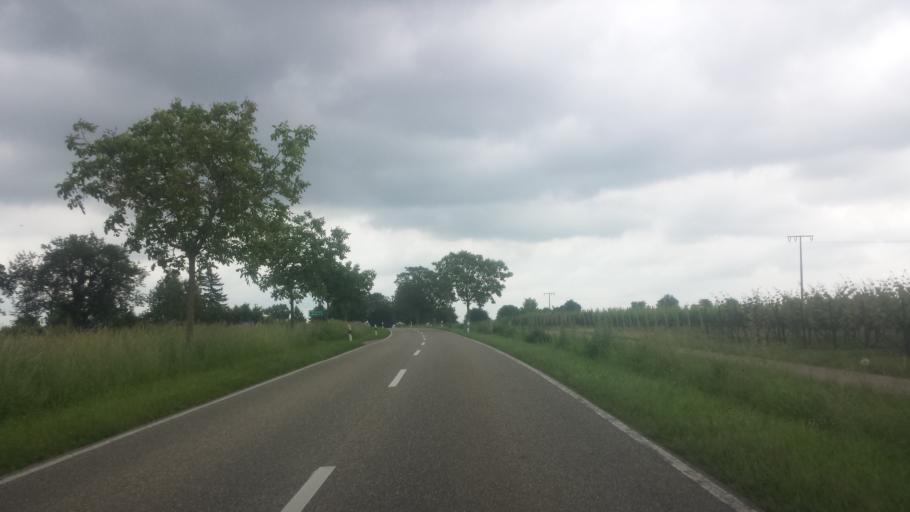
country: DE
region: Rheinland-Pfalz
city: Heuchelheim-Klingen
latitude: 49.1444
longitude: 8.0607
